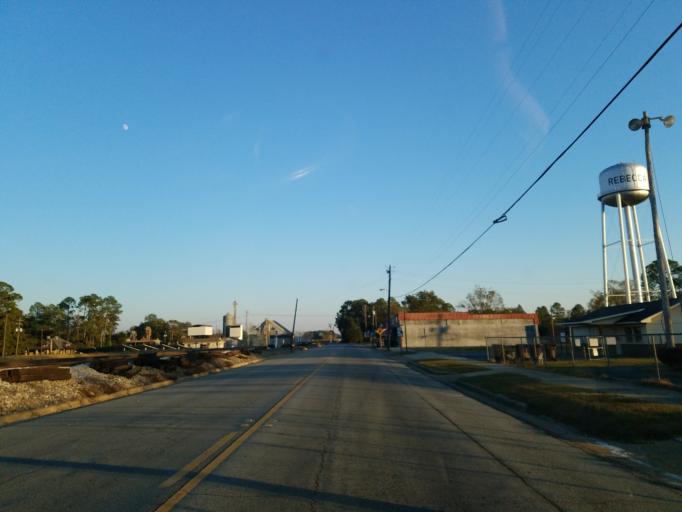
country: US
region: Georgia
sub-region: Wilcox County
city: Rochelle
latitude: 31.8077
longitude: -83.4883
